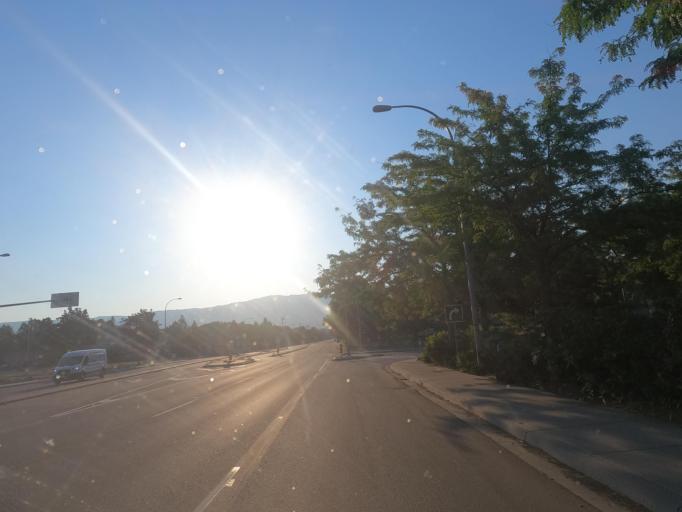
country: CA
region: British Columbia
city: Kelowna
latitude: 49.8889
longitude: -119.4182
